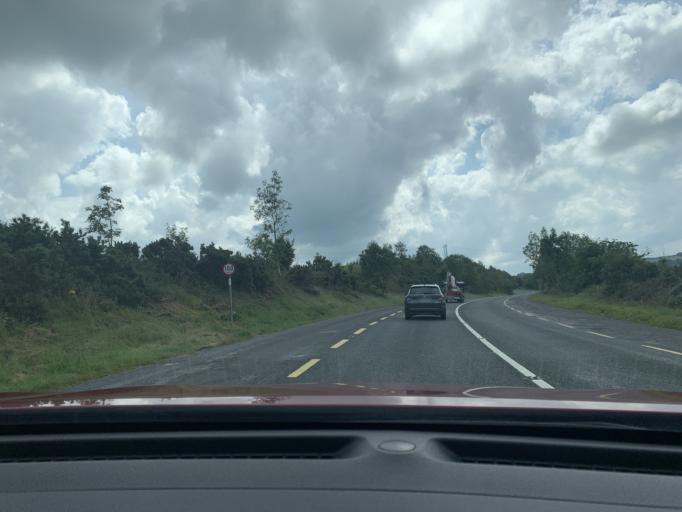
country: IE
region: Connaught
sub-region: Sligo
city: Tobercurry
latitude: 53.9423
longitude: -8.7905
